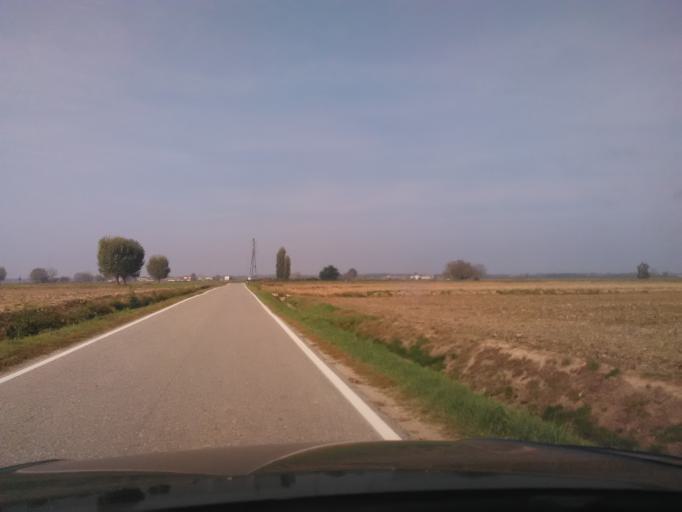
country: IT
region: Piedmont
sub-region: Provincia di Vercelli
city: Tronzano Vercellese
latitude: 45.3502
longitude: 8.1626
